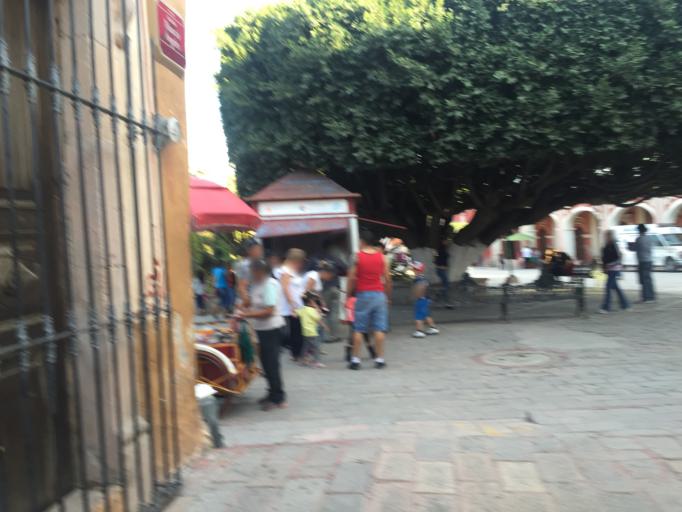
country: MX
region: Queretaro
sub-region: Ezequiel Montes
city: San Jose del Jagueey
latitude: 20.7408
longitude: -99.9415
